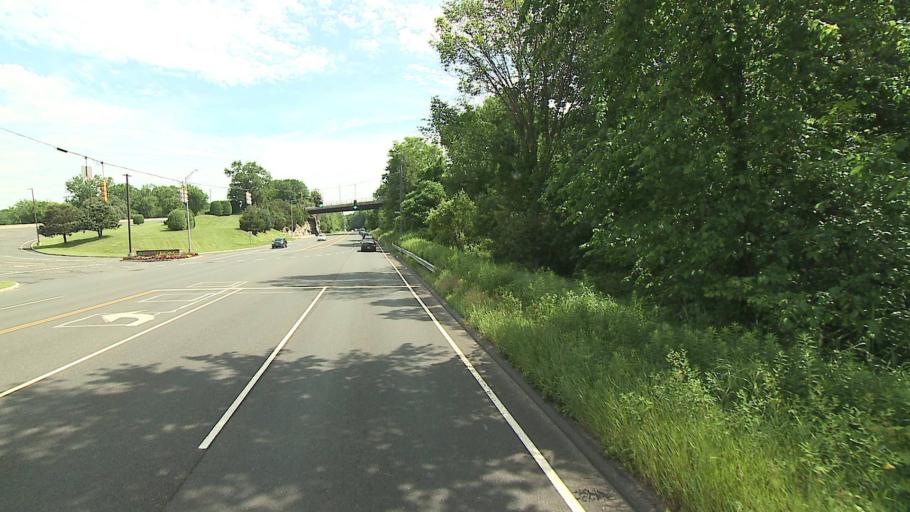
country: US
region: Connecticut
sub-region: Fairfield County
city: Danbury
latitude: 41.4253
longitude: -73.4132
